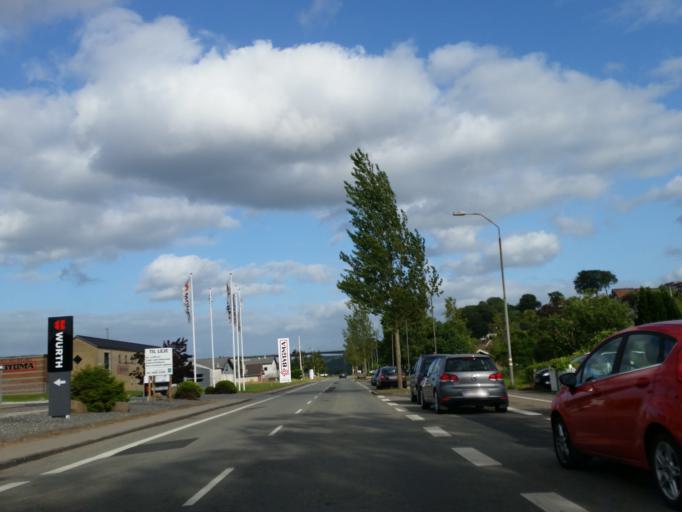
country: DK
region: South Denmark
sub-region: Vejle Kommune
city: Vejle
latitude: 55.7006
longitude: 9.5493
